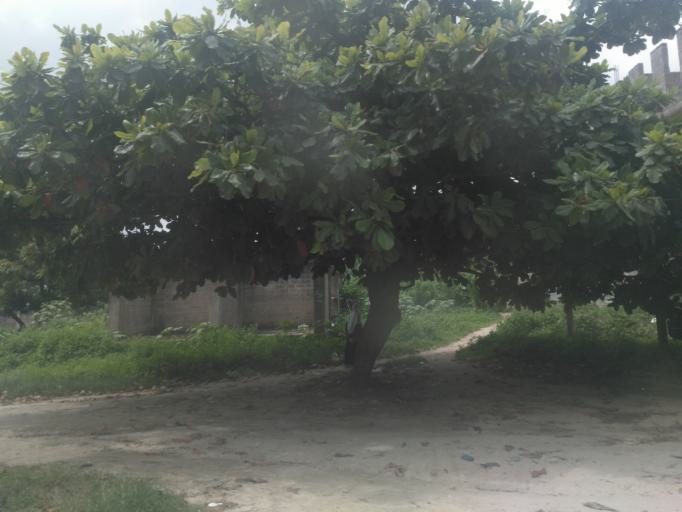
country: TZ
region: Zanzibar Urban/West
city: Zanzibar
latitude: -6.1829
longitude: 39.2224
